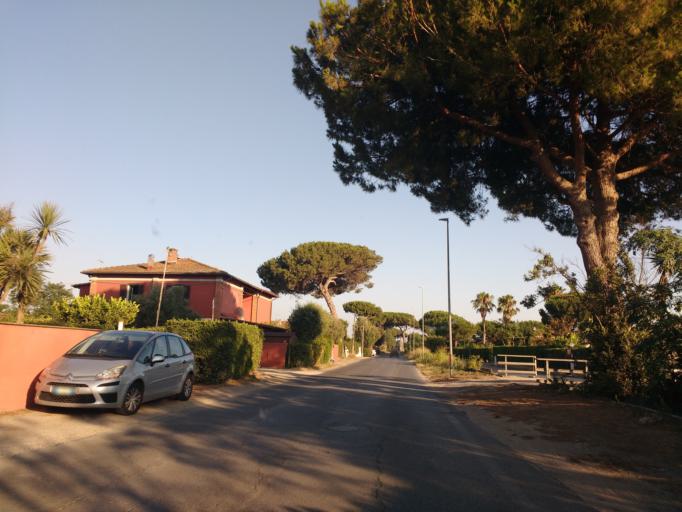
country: IT
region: Latium
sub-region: Citta metropolitana di Roma Capitale
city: Fregene
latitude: 41.8450
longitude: 12.2226
